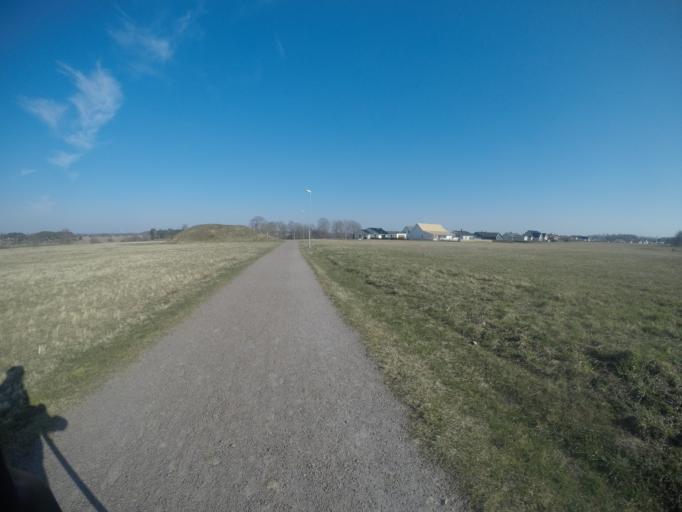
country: SE
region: Halland
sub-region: Laholms Kommun
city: Laholm
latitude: 56.5069
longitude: 13.0637
